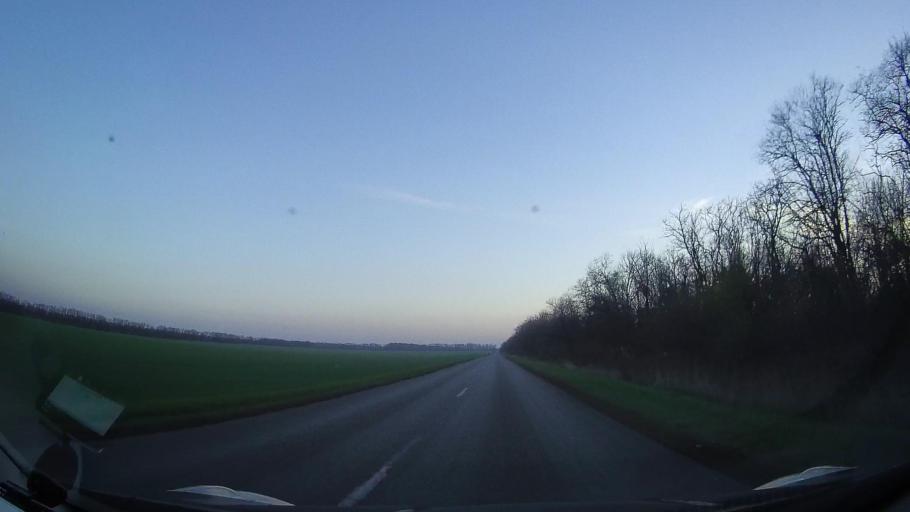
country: RU
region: Rostov
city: Zernograd
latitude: 46.9766
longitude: 40.3915
